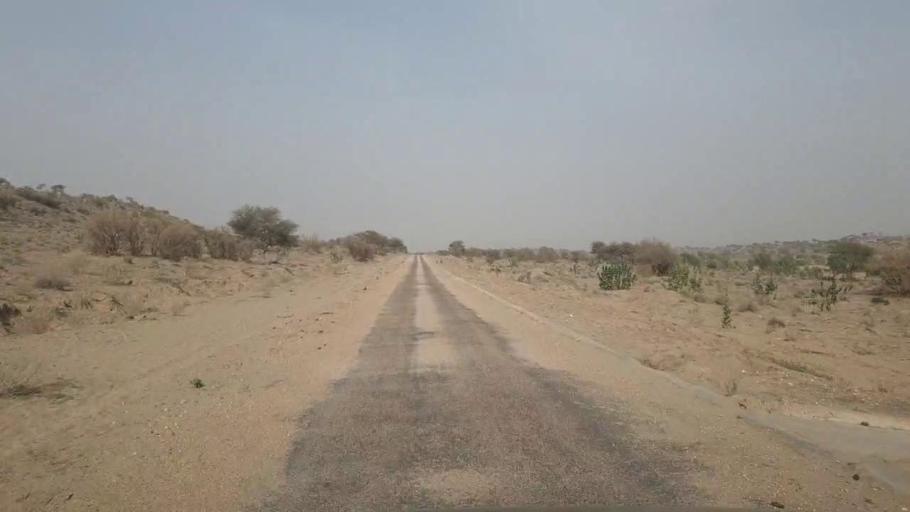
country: PK
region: Sindh
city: Chor
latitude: 25.6345
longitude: 69.9502
